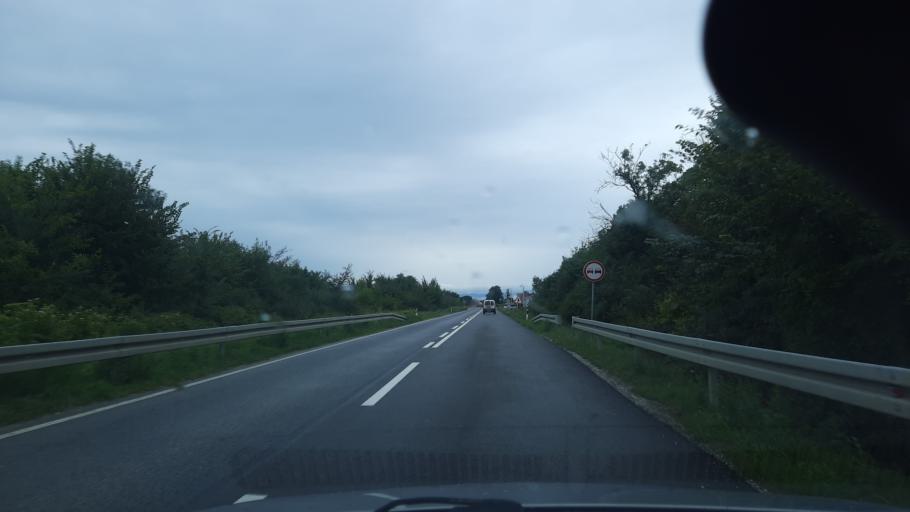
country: RS
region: Central Serbia
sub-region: Sumadijski Okrug
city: Knic
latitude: 43.8149
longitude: 20.7824
